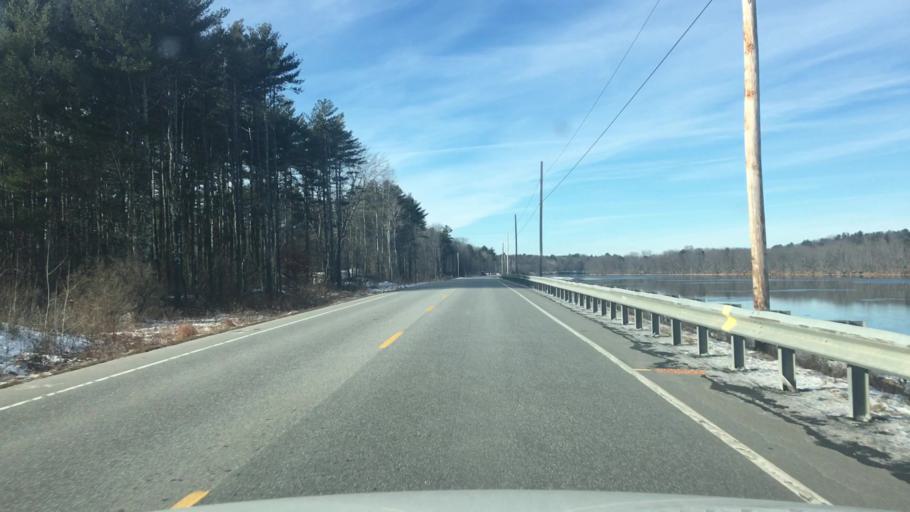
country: US
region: Maine
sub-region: Androscoggin County
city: Lisbon
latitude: 44.0002
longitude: -70.1516
